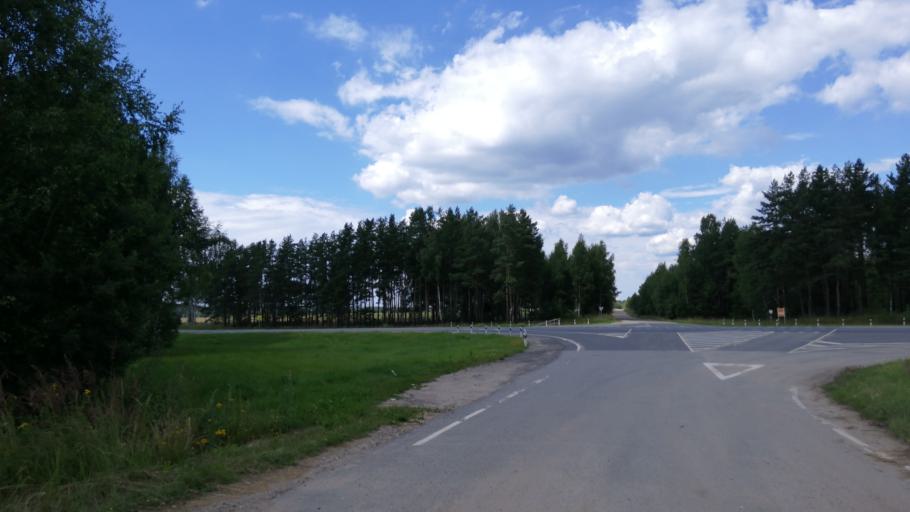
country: RU
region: Jaroslavl
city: Levashevo
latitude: 57.6386
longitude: 40.4614
